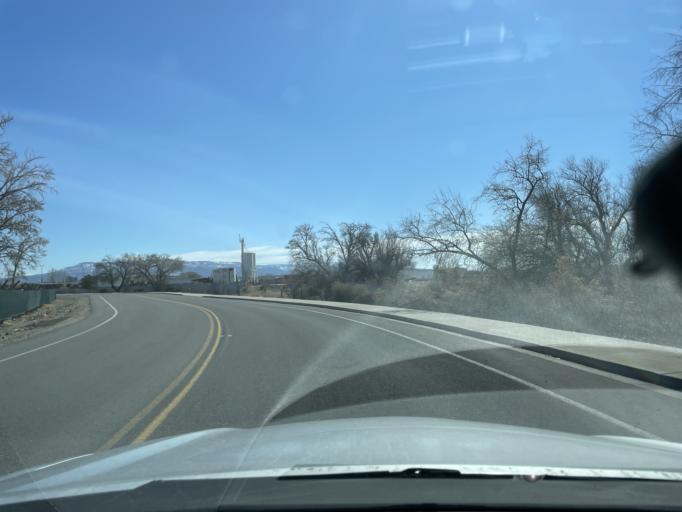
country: US
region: Colorado
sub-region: Mesa County
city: Redlands
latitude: 39.0891
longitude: -108.6107
